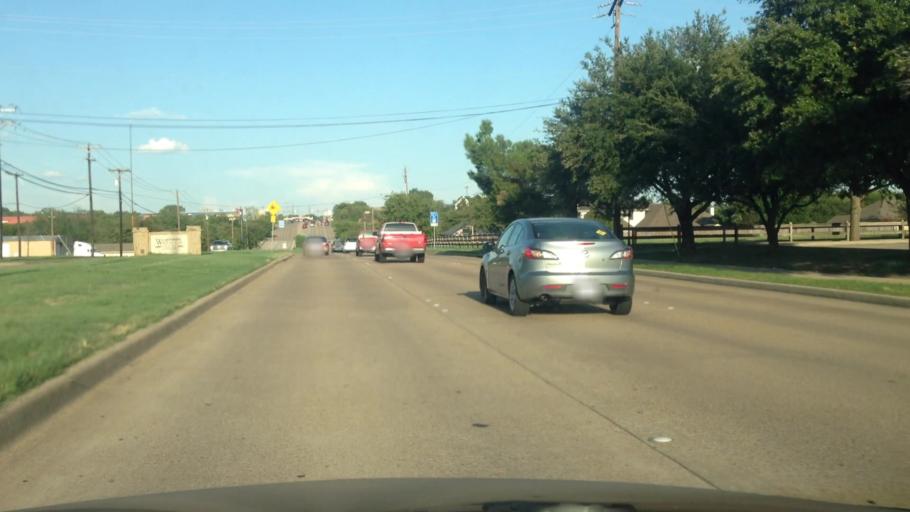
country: US
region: Texas
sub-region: Tarrant County
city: Watauga
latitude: 32.8609
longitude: -97.2731
